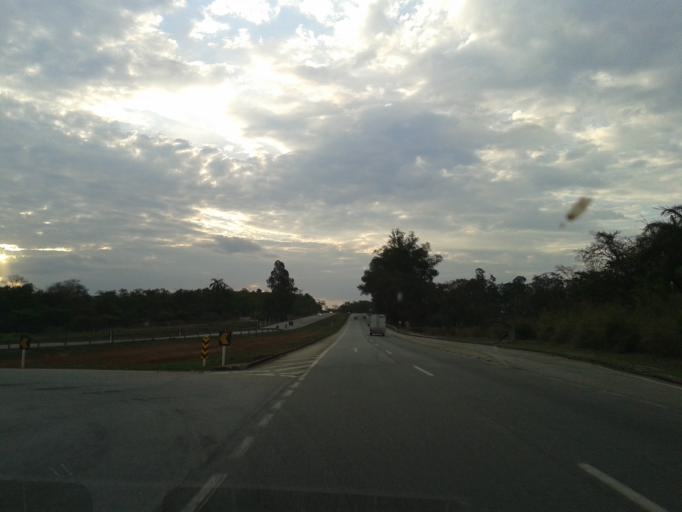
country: BR
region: Minas Gerais
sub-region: Juatuba
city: Juatuba
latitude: -19.9557
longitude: -44.3665
